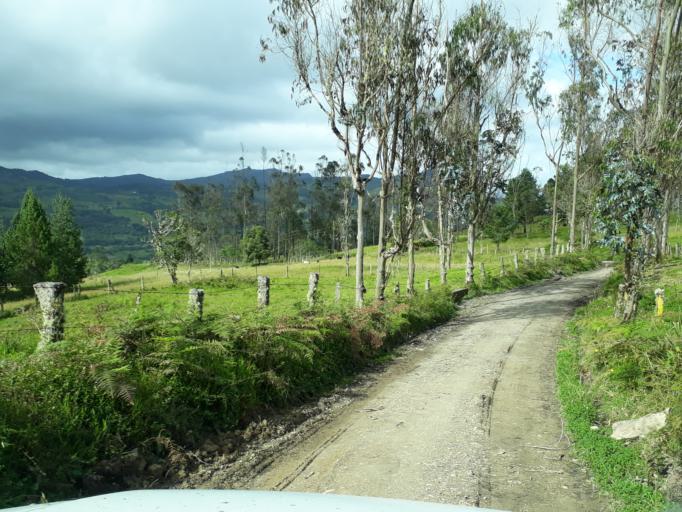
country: CO
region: Cundinamarca
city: Guasca
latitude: 4.8121
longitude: -73.7809
